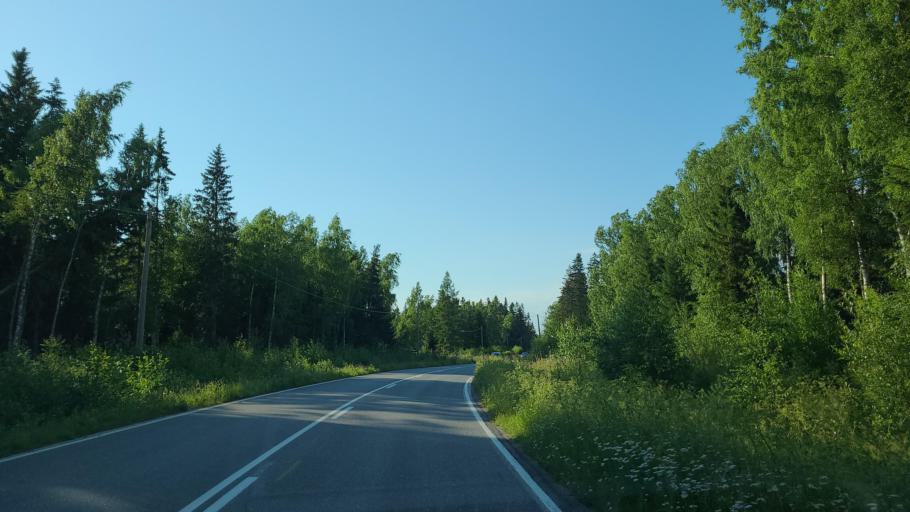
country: FI
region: Ostrobothnia
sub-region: Vaasa
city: Replot
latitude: 63.2669
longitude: 21.3487
